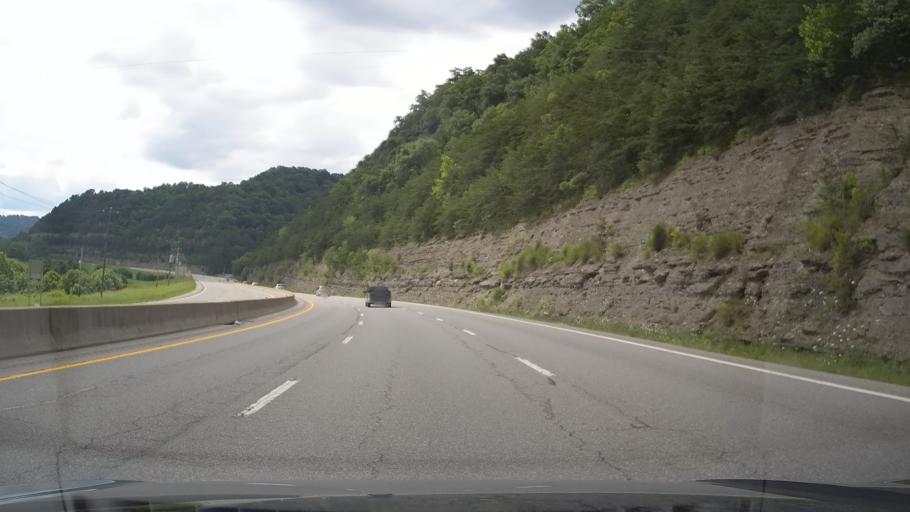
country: US
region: Kentucky
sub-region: Pike County
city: Coal Run Village
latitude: 37.5069
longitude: -82.5332
